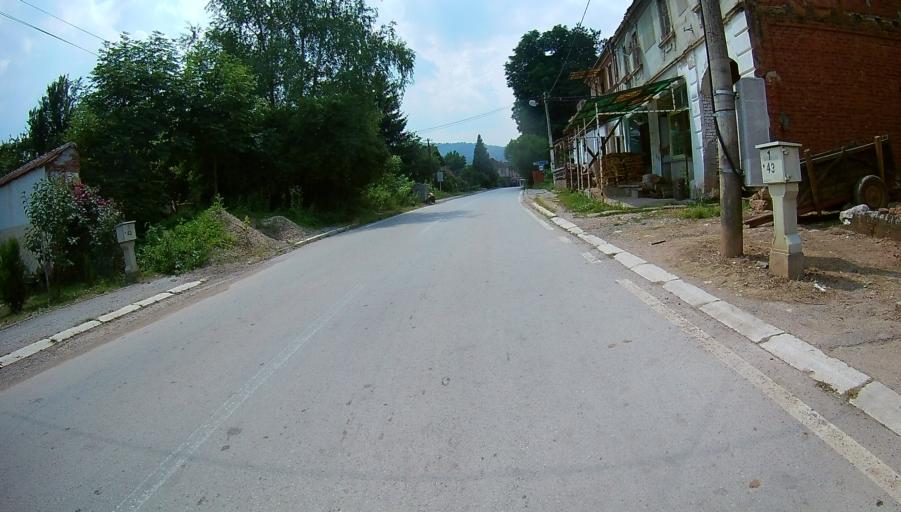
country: RS
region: Central Serbia
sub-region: Nisavski Okrug
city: Gadzin Han
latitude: 43.1628
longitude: 22.1086
